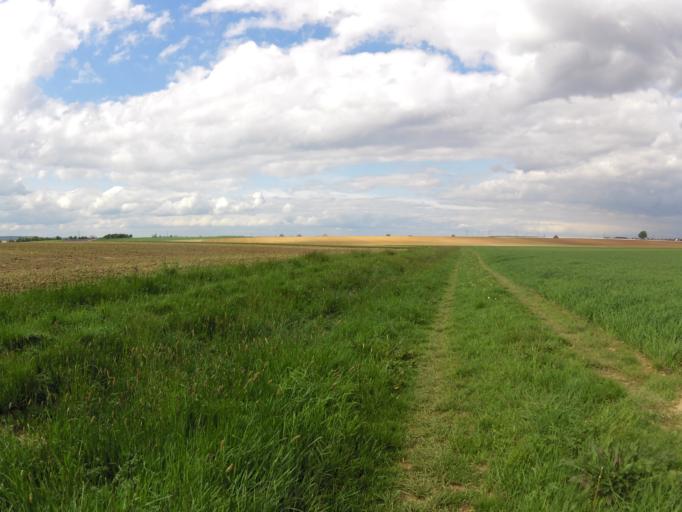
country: DE
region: Bavaria
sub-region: Regierungsbezirk Unterfranken
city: Oberpleichfeld
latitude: 49.8618
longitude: 10.0717
